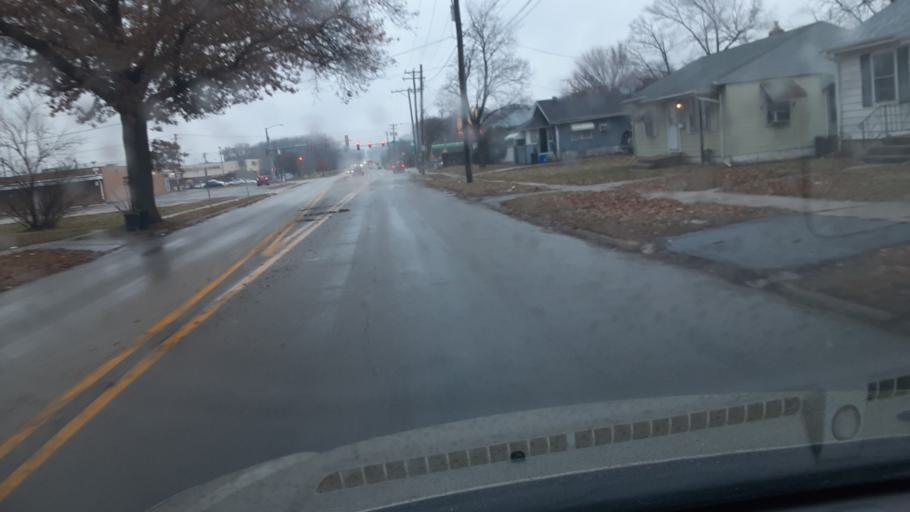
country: US
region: Illinois
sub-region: Winnebago County
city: Rockford
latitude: 42.2869
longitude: -89.1161
